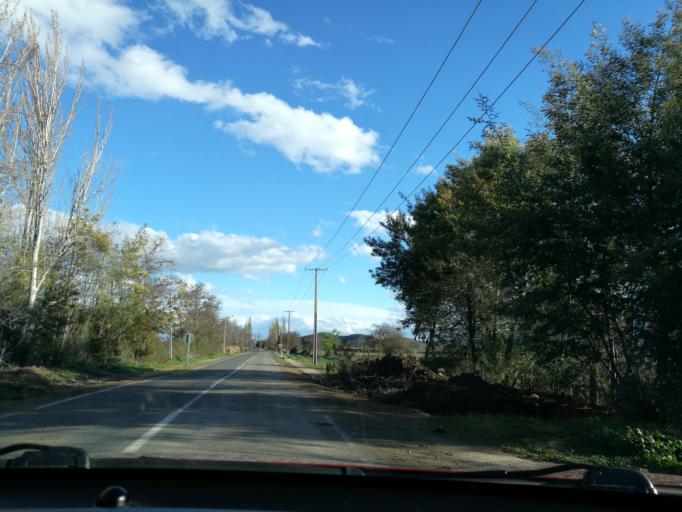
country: CL
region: O'Higgins
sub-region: Provincia de Cachapoal
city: Graneros
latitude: -34.1032
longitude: -70.8094
